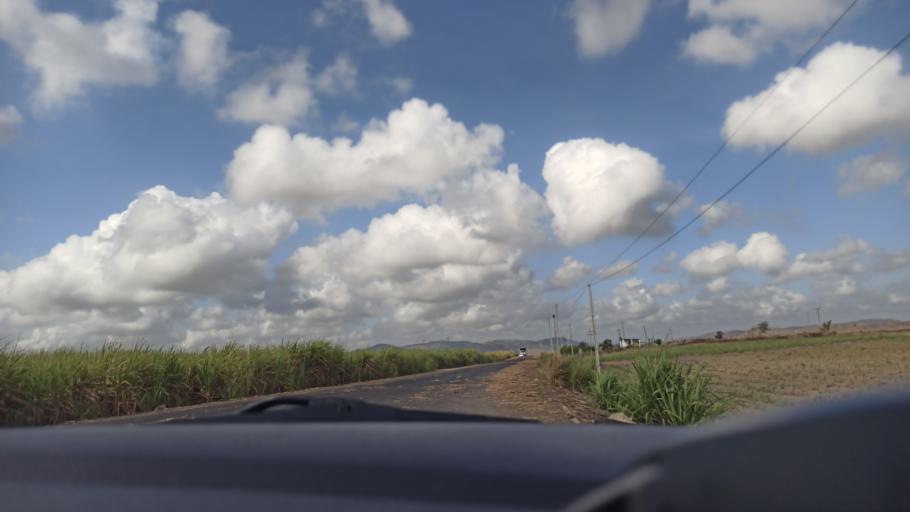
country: BR
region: Paraiba
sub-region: Juripiranga
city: Juripiranga
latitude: -7.3848
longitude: -35.2482
